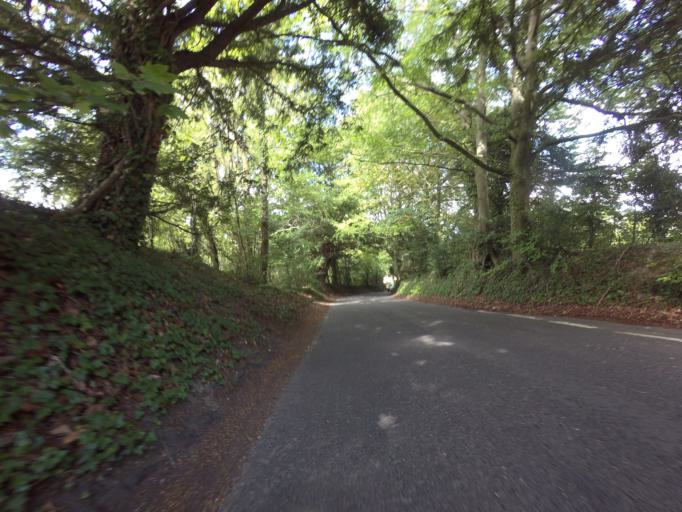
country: GB
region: England
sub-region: Kent
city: Shoreham
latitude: 51.3415
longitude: 0.1765
